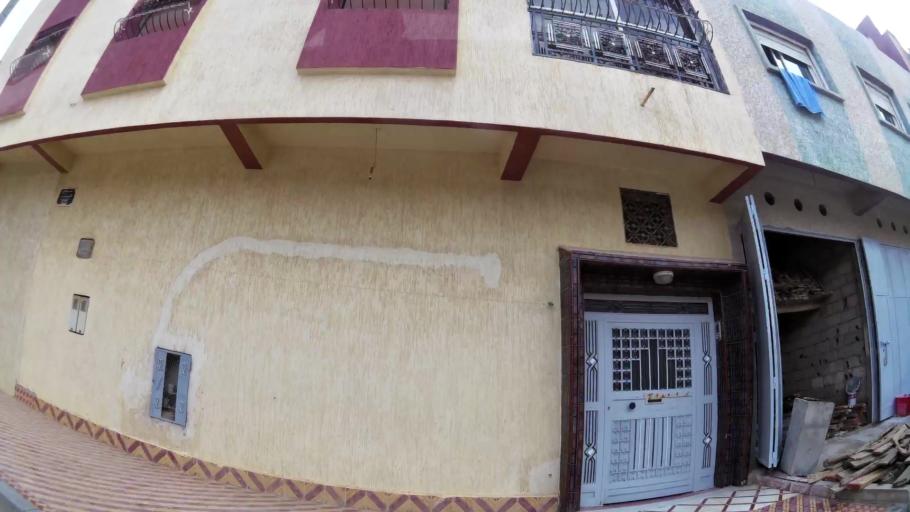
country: MA
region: Rabat-Sale-Zemmour-Zaer
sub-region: Khemisset
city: Tiflet
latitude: 33.8908
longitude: -6.3263
